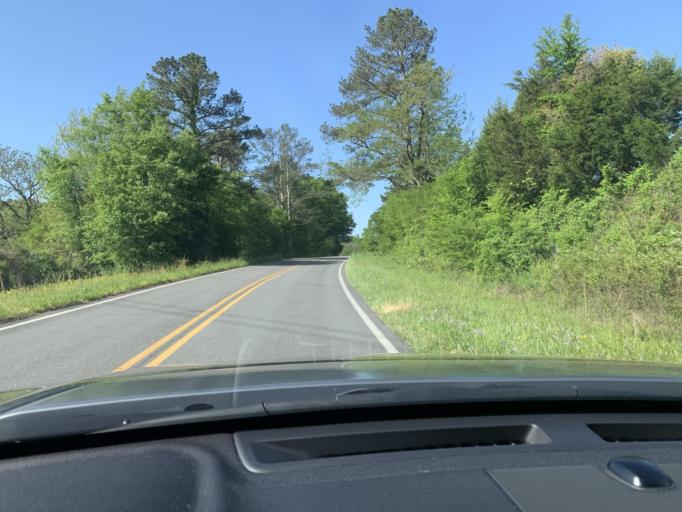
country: US
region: Georgia
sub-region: Polk County
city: Cedartown
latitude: 34.0453
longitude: -85.3000
